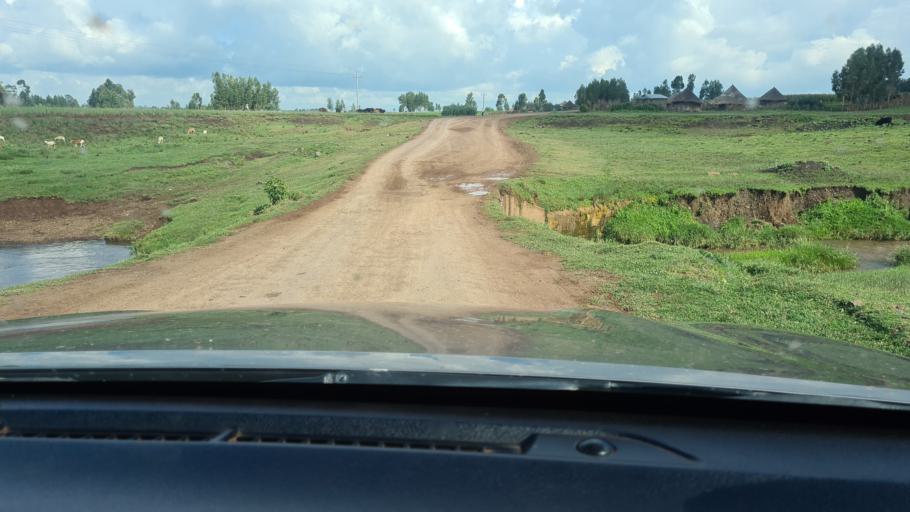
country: ET
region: Oromiya
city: Huruta
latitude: 7.9355
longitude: 39.6018
